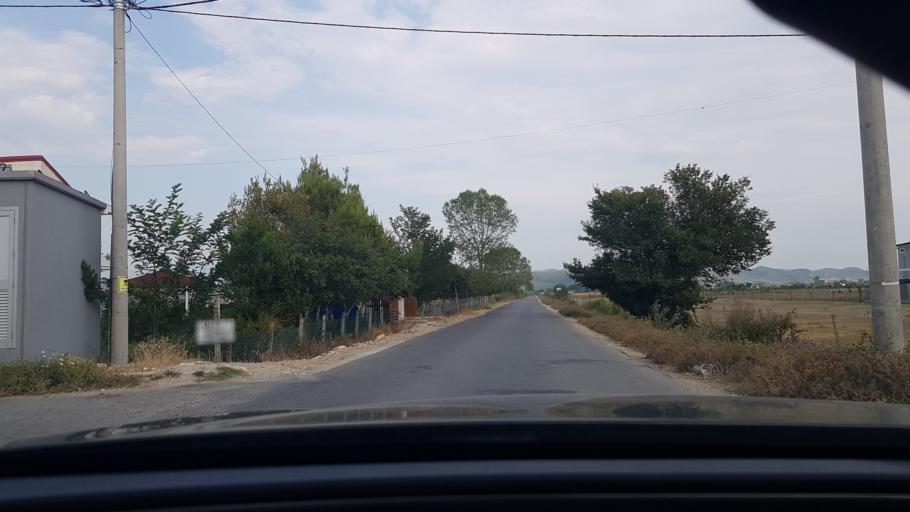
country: AL
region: Durres
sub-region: Rrethi i Durresit
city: Katundi i Ri
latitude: 41.4845
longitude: 19.5286
